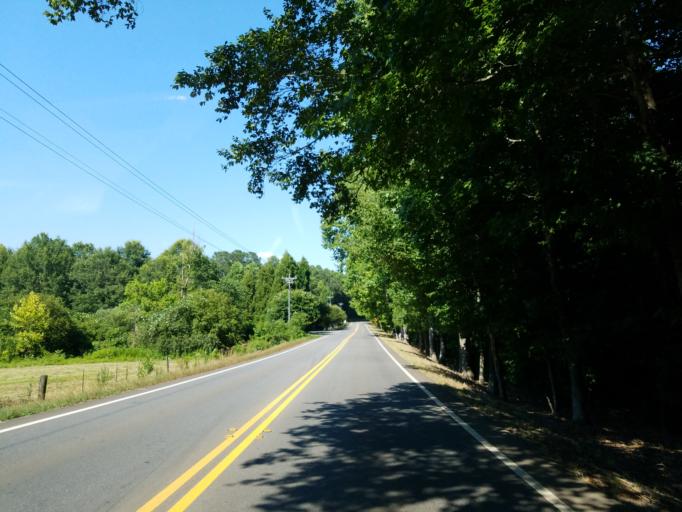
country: US
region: Georgia
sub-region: Fulton County
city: Milton
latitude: 34.1917
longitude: -84.3129
